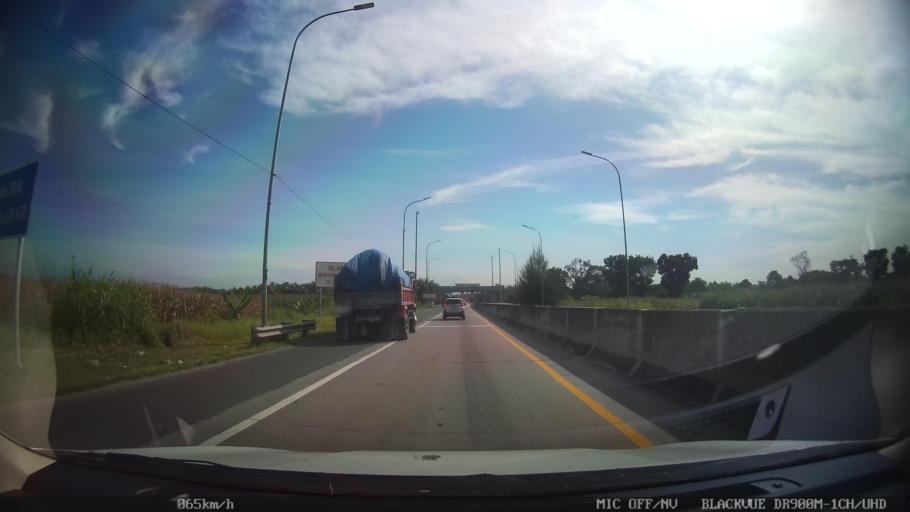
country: ID
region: North Sumatra
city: Sunggal
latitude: 3.6280
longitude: 98.6305
